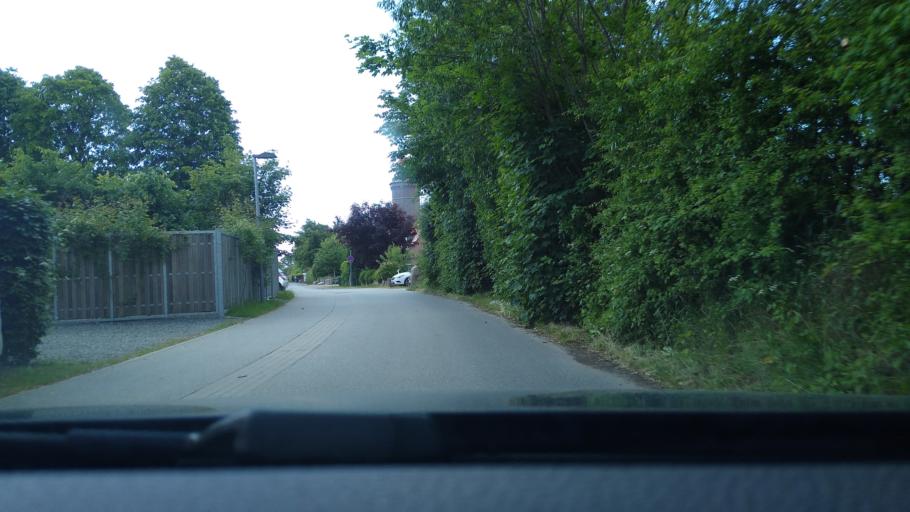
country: DE
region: Schleswig-Holstein
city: Dahme
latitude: 54.2033
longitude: 11.0899
